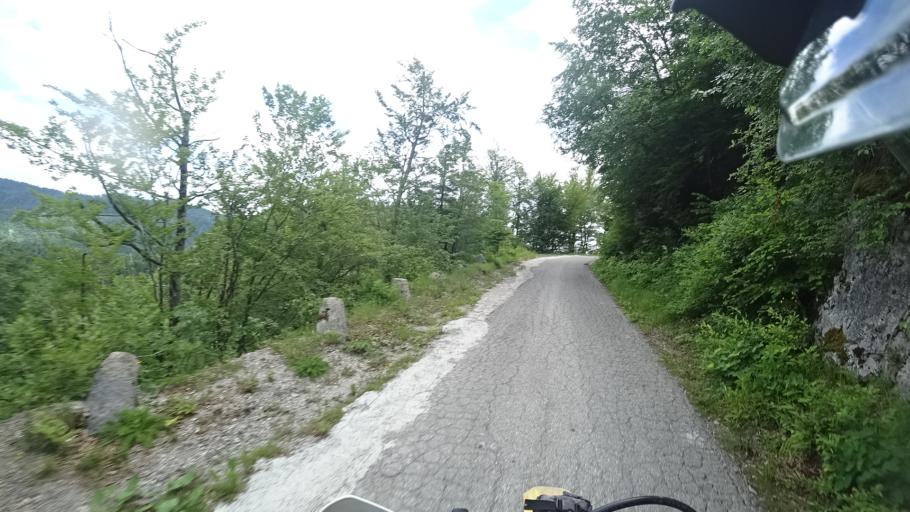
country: SI
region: Osilnica
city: Osilnica
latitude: 45.5974
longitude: 14.6294
